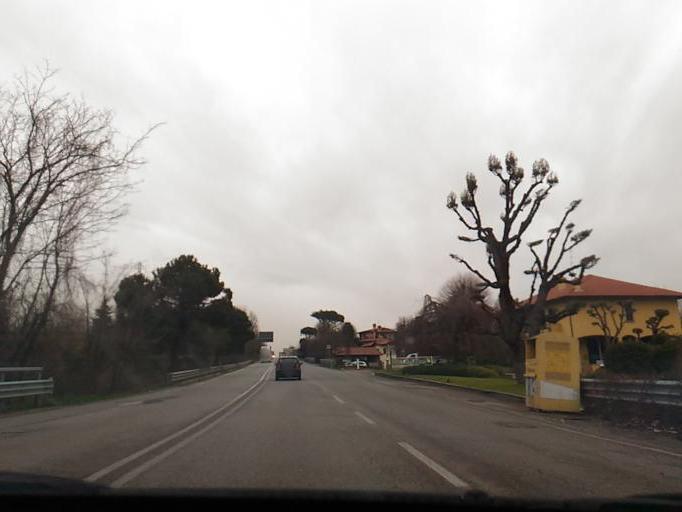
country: IT
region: Lombardy
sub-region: Provincia di Como
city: Mariano Comense
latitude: 45.7089
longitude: 9.1724
